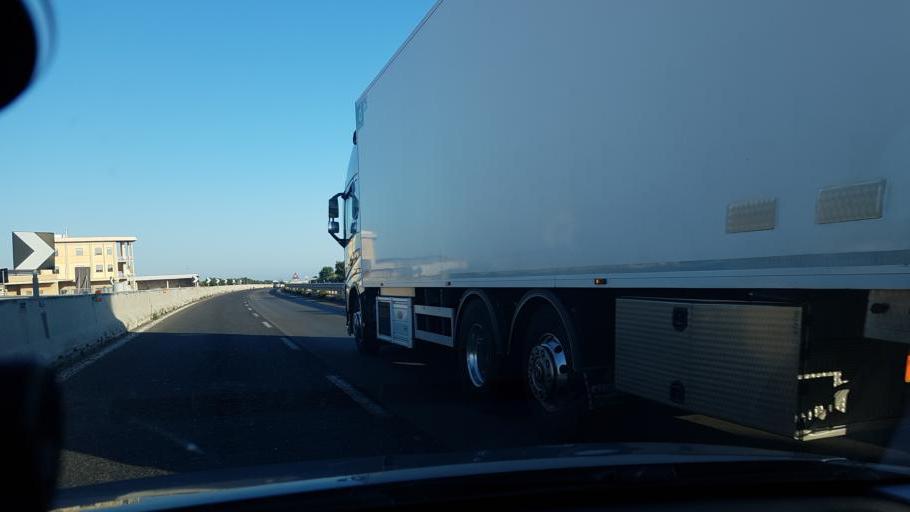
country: IT
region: Apulia
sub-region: Provincia di Brindisi
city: Fasano
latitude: 40.8581
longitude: 17.3501
